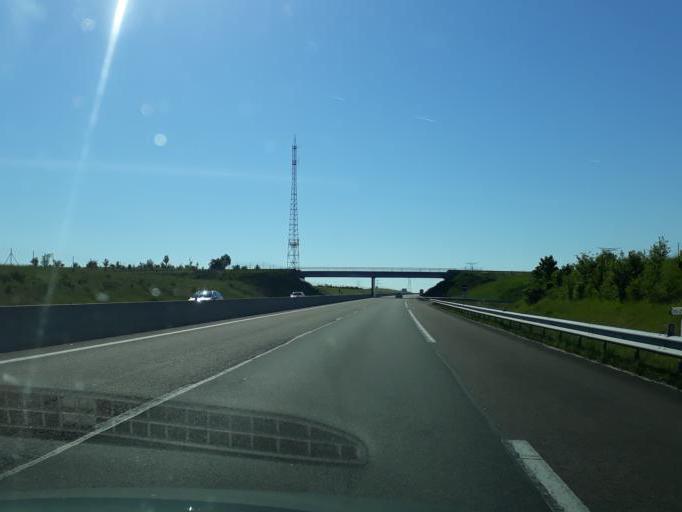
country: FR
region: Centre
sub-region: Departement du Loiret
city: Boynes
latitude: 48.1072
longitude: 2.3182
